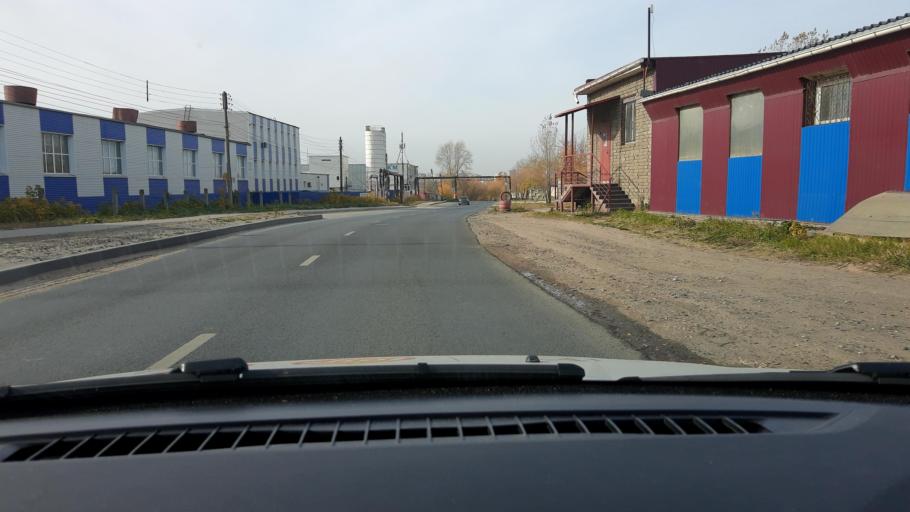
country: RU
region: Nizjnij Novgorod
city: Bor
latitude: 56.3066
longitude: 44.0586
